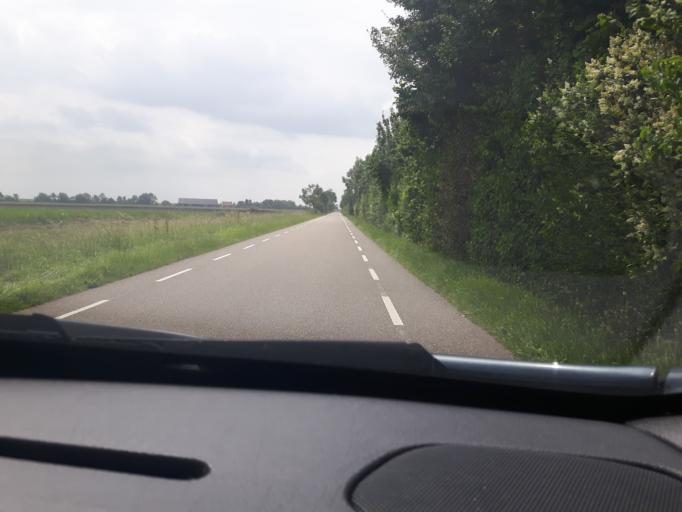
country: NL
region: Zeeland
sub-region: Gemeente Terneuzen
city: Terneuzen
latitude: 51.4058
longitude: 3.8404
